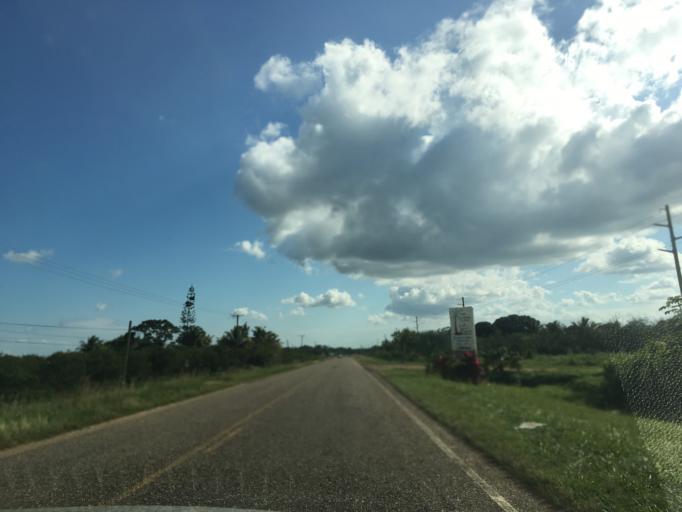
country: BZ
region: Stann Creek
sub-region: Dangriga
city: Dangriga
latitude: 16.8591
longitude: -88.3467
